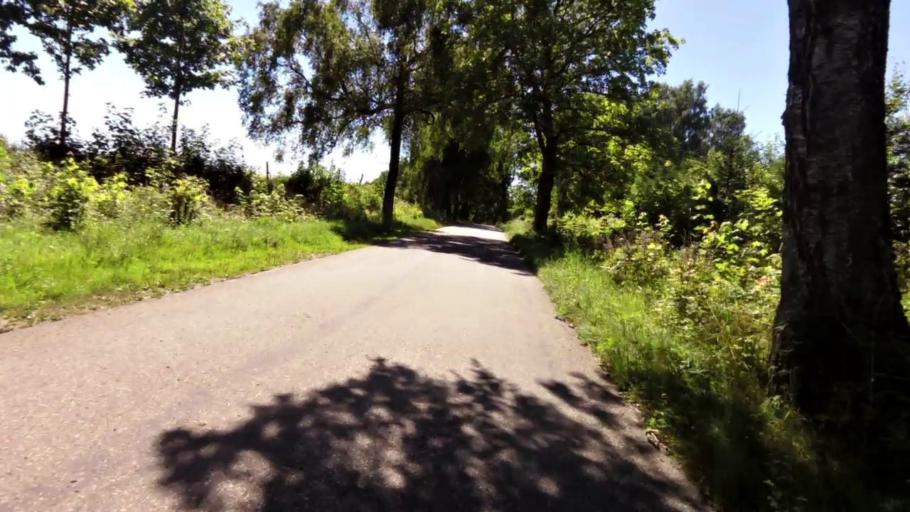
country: PL
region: West Pomeranian Voivodeship
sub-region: Powiat szczecinecki
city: Bialy Bor
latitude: 53.9720
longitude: 16.8653
